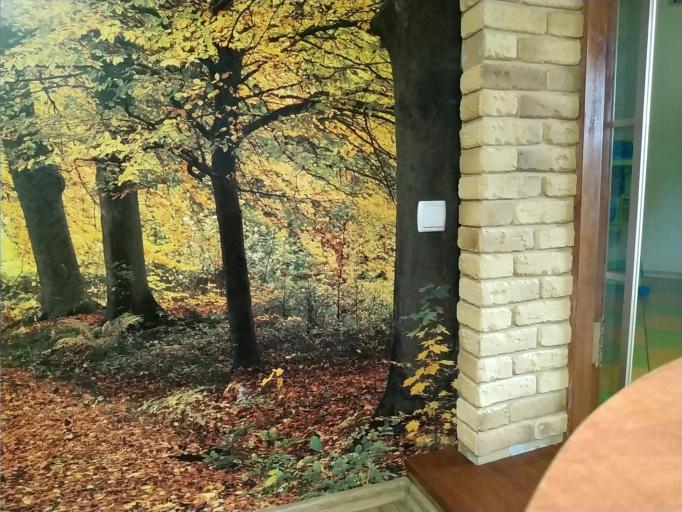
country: RU
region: Smolensk
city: Dorogobuzh
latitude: 54.9279
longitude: 33.3223
